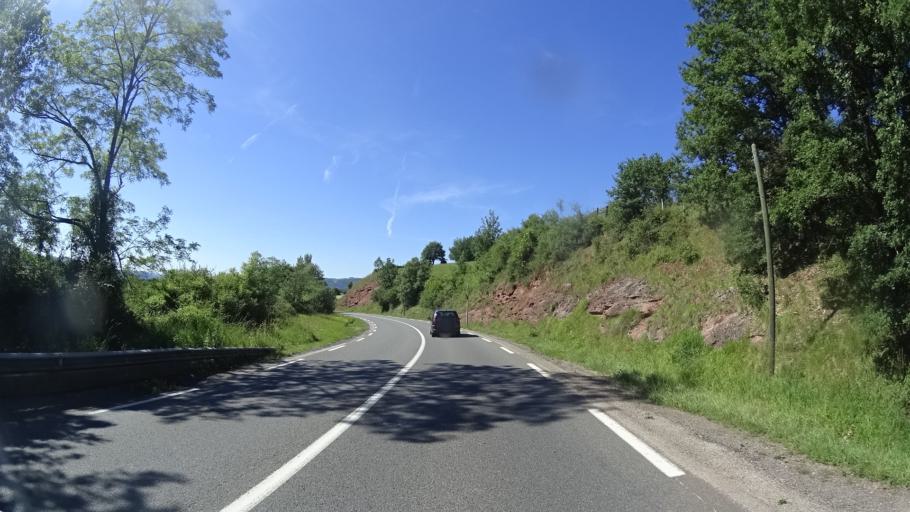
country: FR
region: Midi-Pyrenees
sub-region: Departement de l'Aveyron
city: Firmi
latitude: 44.5096
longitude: 2.3619
